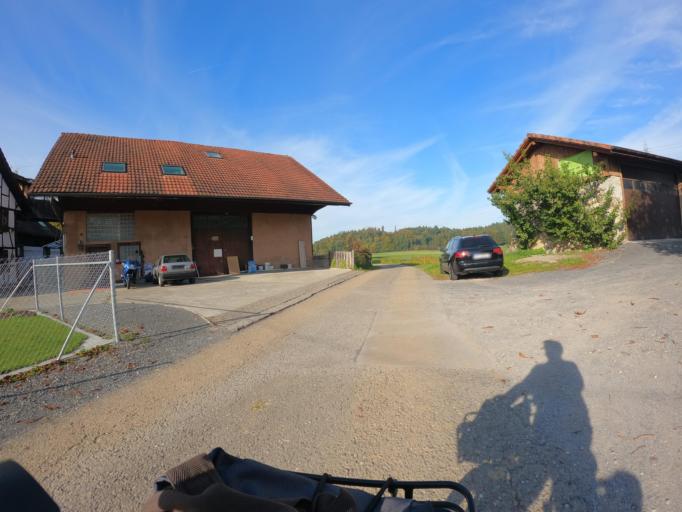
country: CH
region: Aargau
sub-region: Bezirk Muri
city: Muri
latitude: 47.2853
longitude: 8.3425
